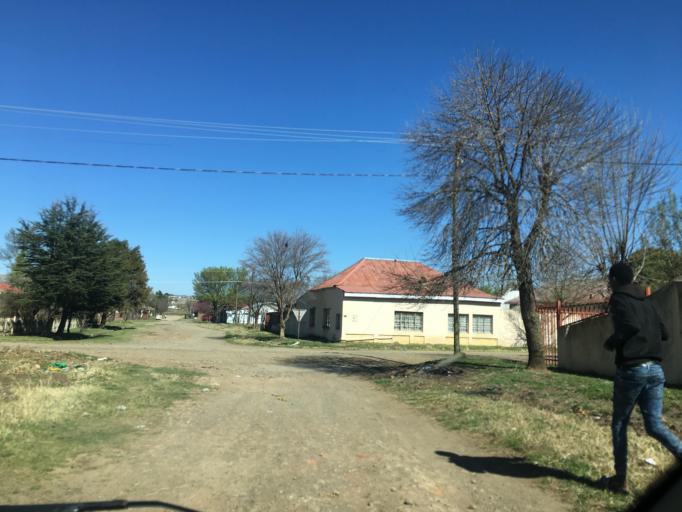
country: ZA
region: Eastern Cape
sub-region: Chris Hani District Municipality
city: Elliot
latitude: -31.3360
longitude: 27.8505
